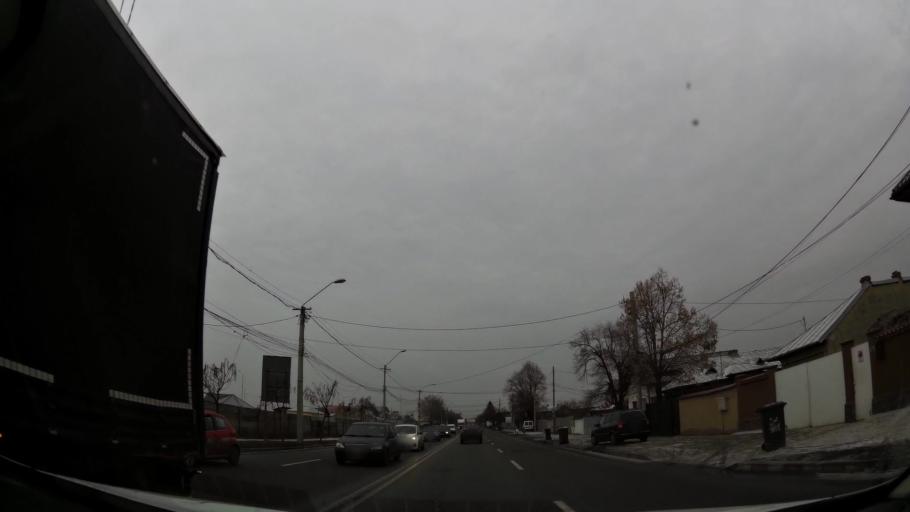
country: RO
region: Dambovita
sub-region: Comuna Ulmi
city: Ulmi
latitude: 44.9075
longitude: 25.4911
